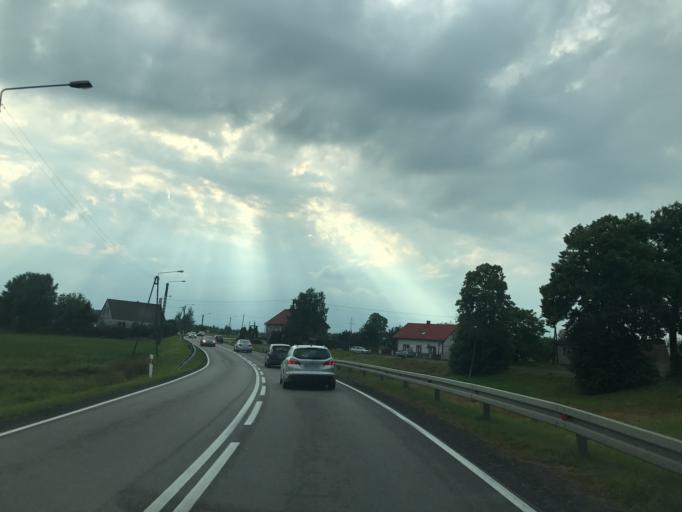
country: PL
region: Pomeranian Voivodeship
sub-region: Powiat czluchowski
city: Czluchow
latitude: 53.6865
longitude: 17.3273
